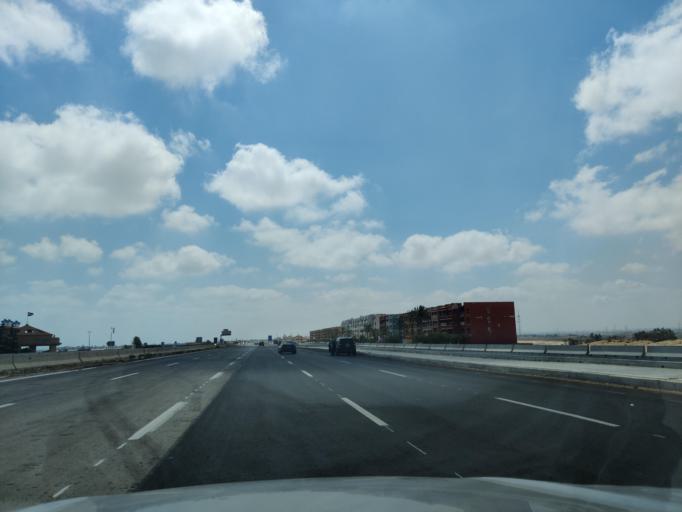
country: EG
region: Muhafazat Matruh
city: Al `Alamayn
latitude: 30.8216
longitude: 28.9966
